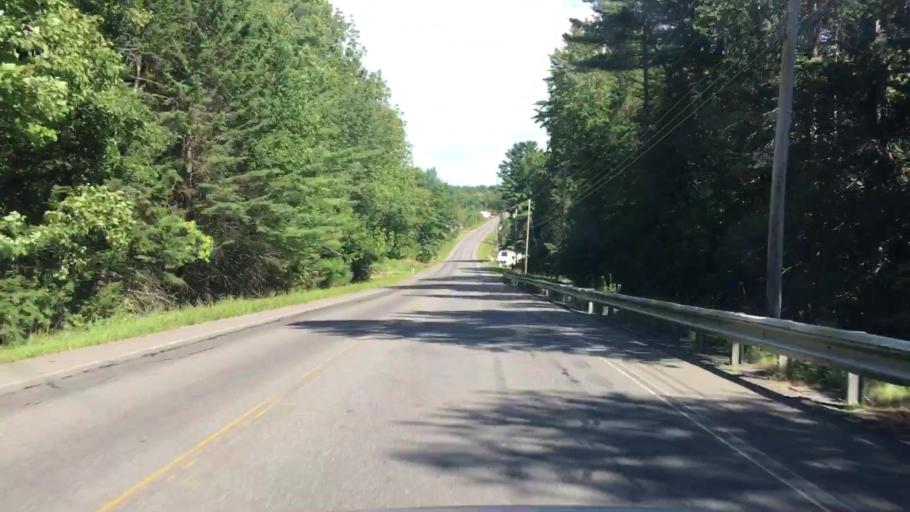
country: US
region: Maine
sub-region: Penobscot County
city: Dexter
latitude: 45.0774
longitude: -69.2311
